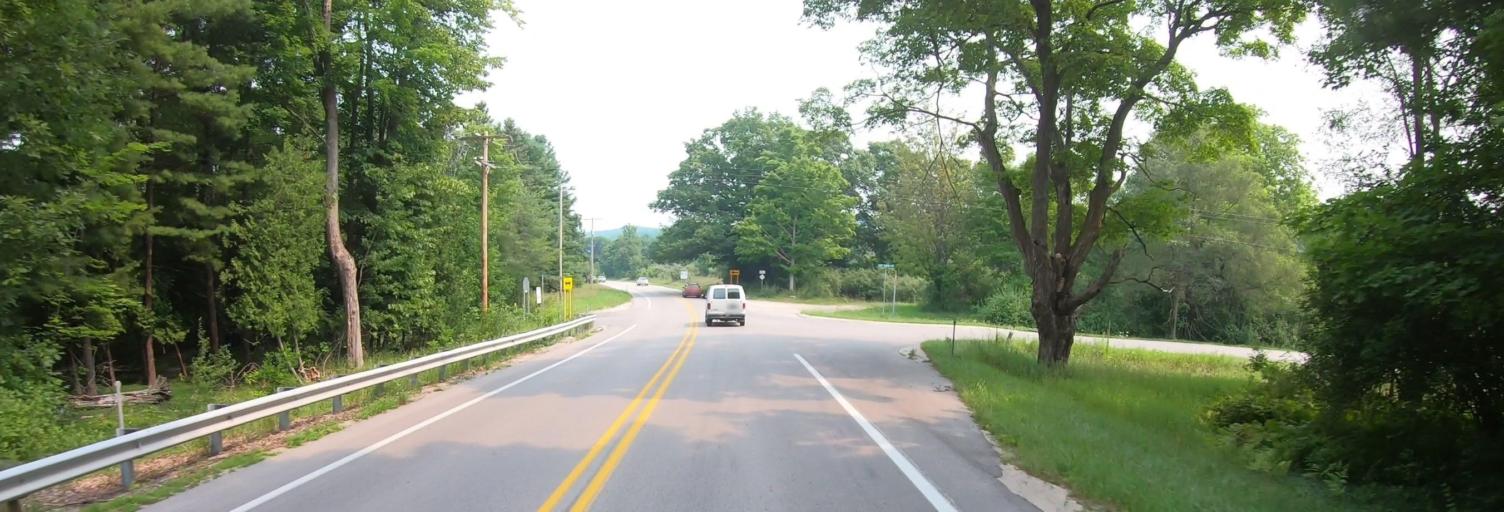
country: US
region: Michigan
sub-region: Leelanau County
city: Leland
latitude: 44.9438
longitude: -85.8027
